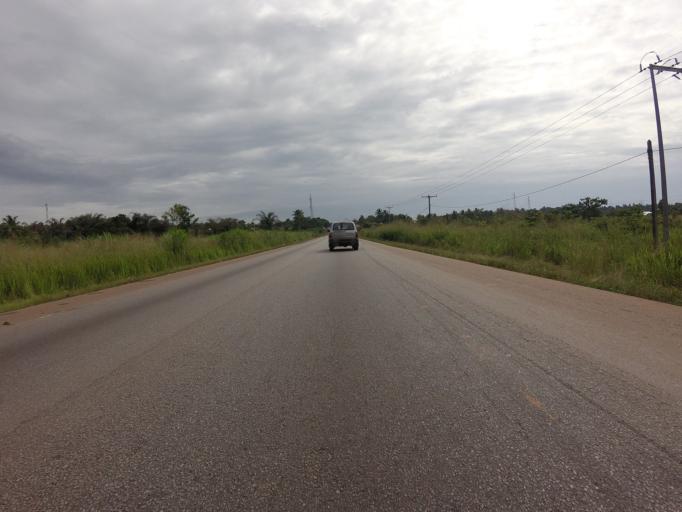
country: GH
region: Eastern
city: Nkawkaw
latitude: 6.5996
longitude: -0.8900
